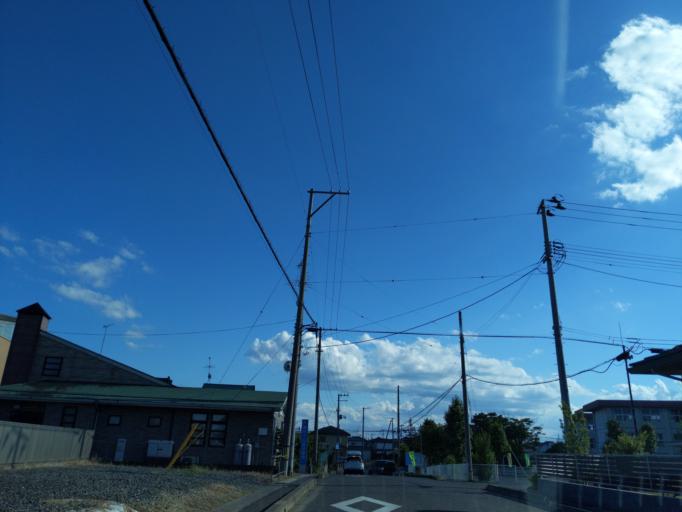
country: JP
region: Fukushima
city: Koriyama
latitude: 37.3813
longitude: 140.3342
